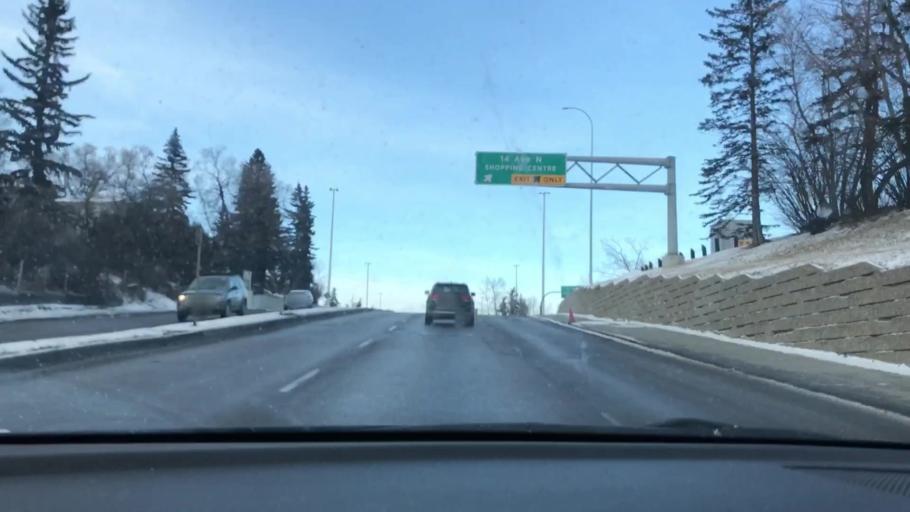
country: CA
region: Alberta
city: Calgary
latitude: 51.0622
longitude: -114.0946
